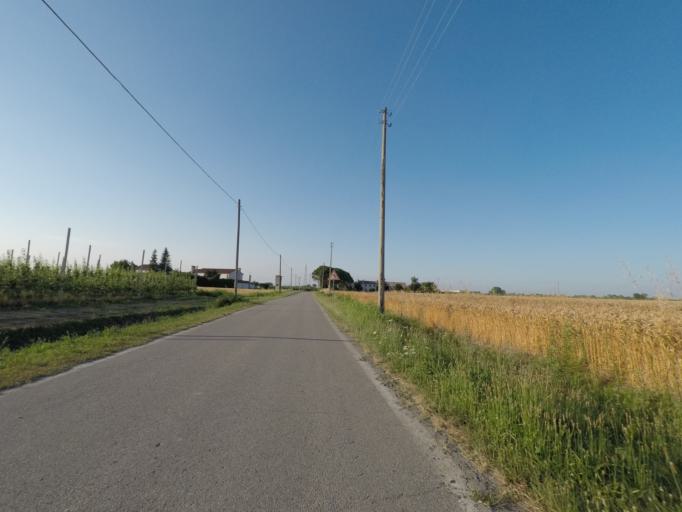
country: IT
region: Veneto
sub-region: Provincia di Rovigo
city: Villamarzana
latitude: 45.0292
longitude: 11.6771
